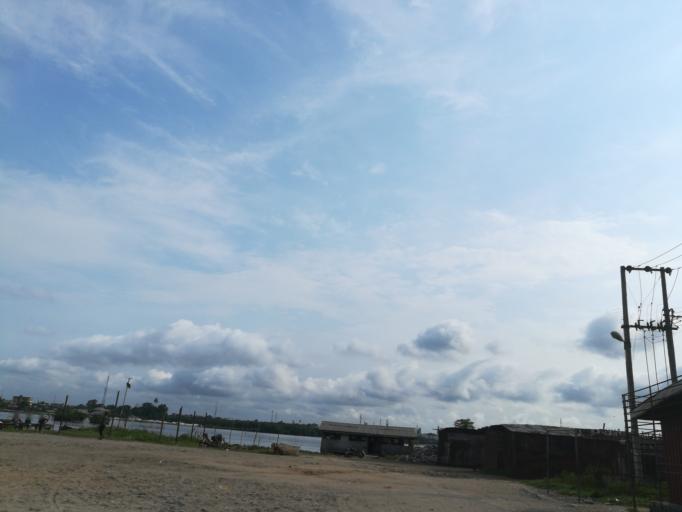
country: NG
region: Rivers
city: Okrika
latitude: 4.7448
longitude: 7.0895
